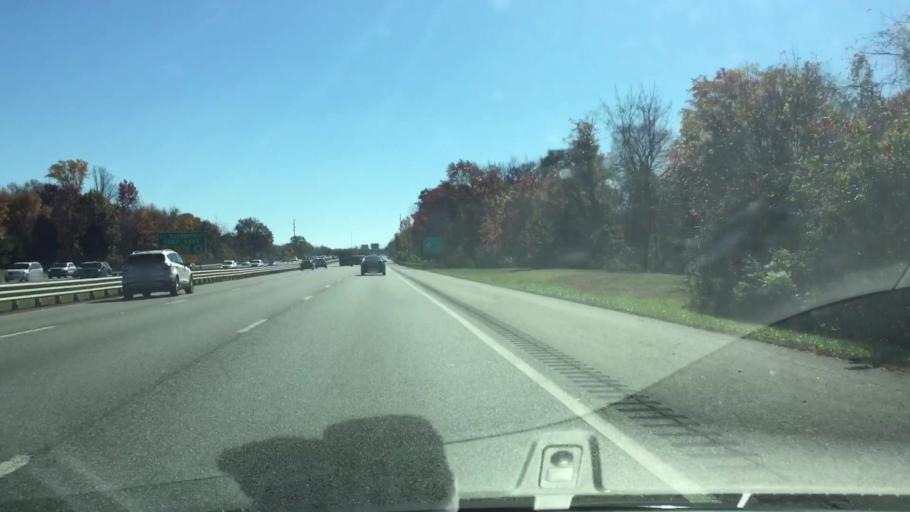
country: US
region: New Jersey
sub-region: Gloucester County
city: Turnersville
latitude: 39.7764
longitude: -75.0490
